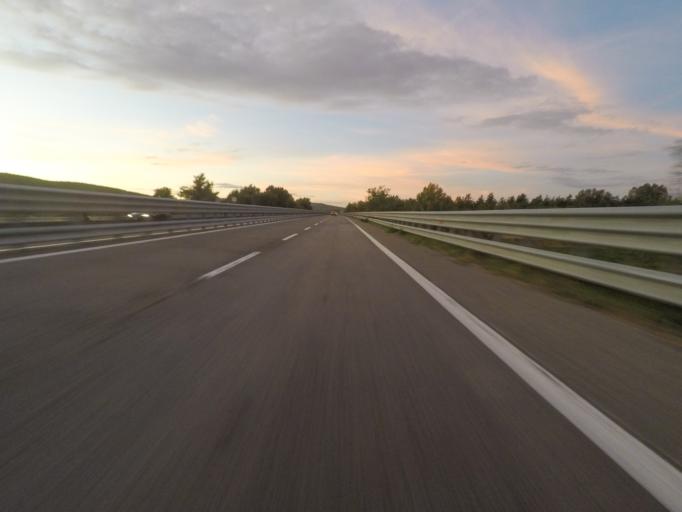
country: IT
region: Tuscany
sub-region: Provincia di Siena
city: Sinalunga
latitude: 43.2426
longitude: 11.7230
